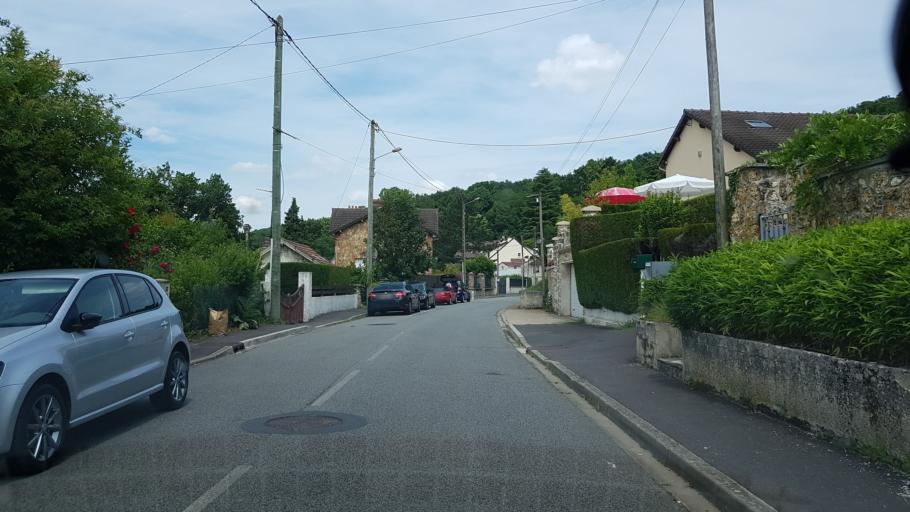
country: FR
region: Ile-de-France
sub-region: Departement des Yvelines
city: Saint-Remy-les-Chevreuse
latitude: 48.7149
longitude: 2.0690
